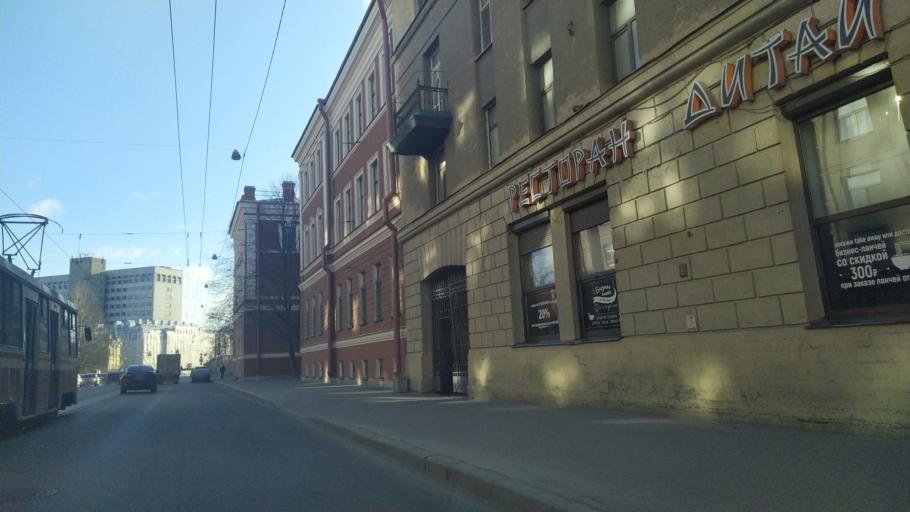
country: RU
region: Leningrad
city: Finlyandskiy
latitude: 59.9620
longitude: 30.3524
